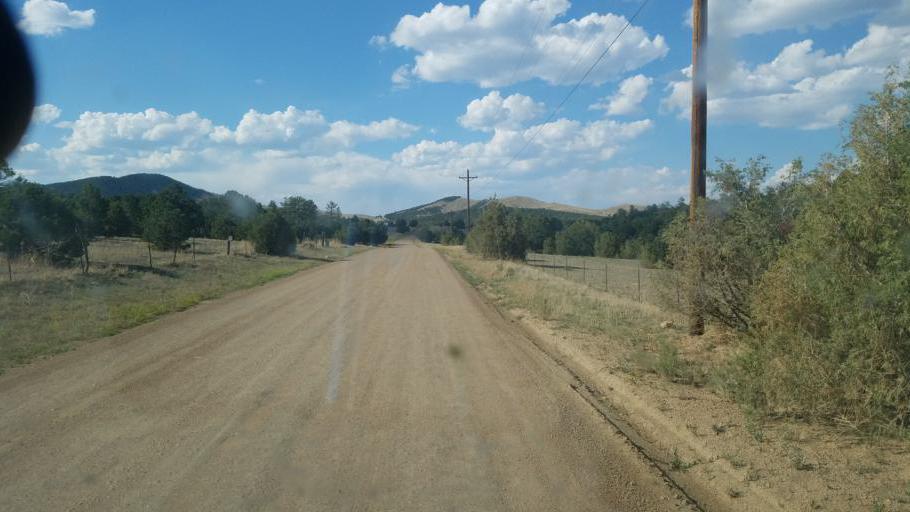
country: US
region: Colorado
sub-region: Custer County
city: Westcliffe
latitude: 38.3005
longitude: -105.4865
